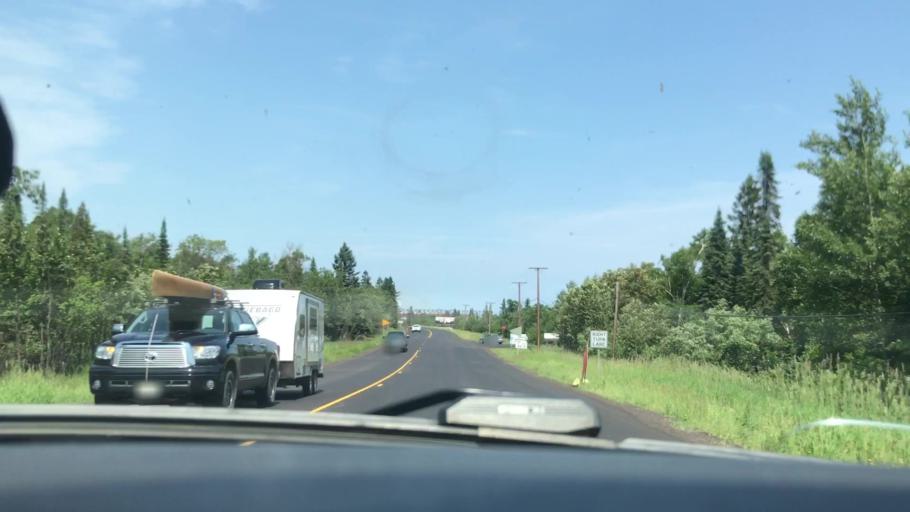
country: US
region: Minnesota
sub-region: Lake County
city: Silver Bay
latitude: 47.2715
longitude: -91.2792
